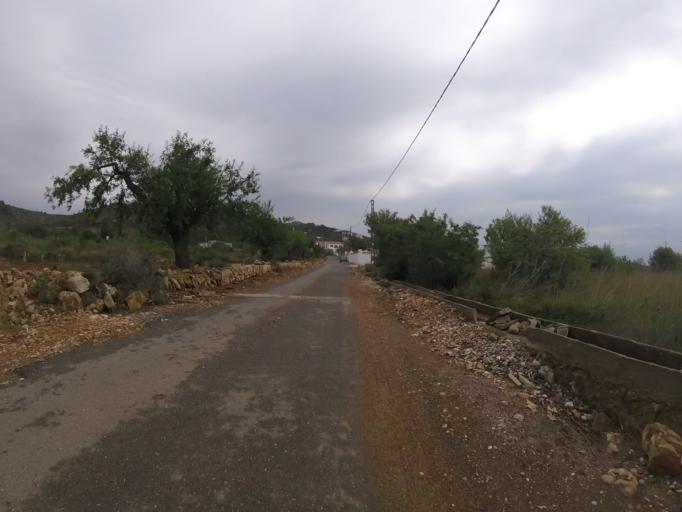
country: ES
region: Valencia
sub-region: Provincia de Castello
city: Alcoceber
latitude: 40.2464
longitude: 0.2552
